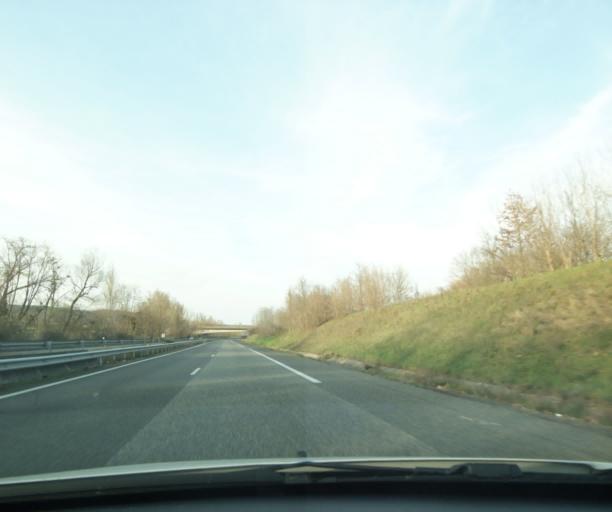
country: FR
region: Midi-Pyrenees
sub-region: Departement de la Haute-Garonne
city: Martres-Tolosane
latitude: 43.1671
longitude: 0.9724
